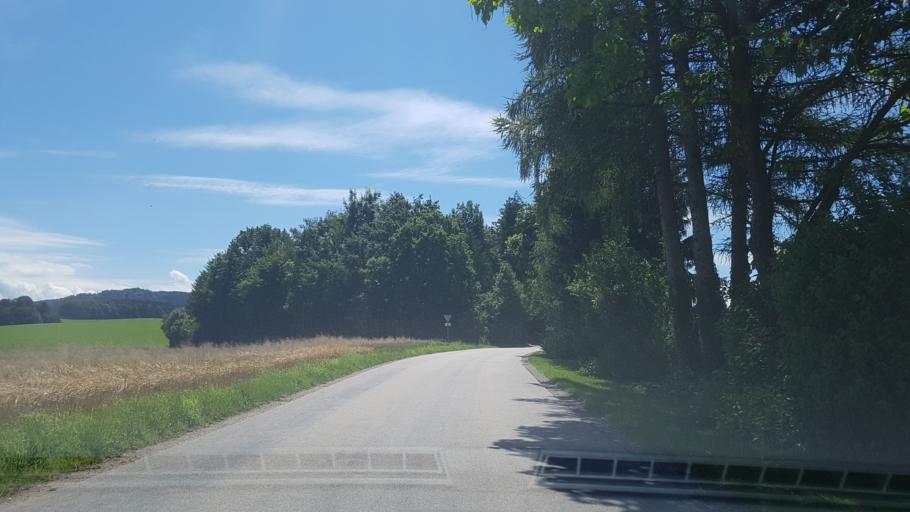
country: AT
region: Salzburg
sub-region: Politischer Bezirk Salzburg-Umgebung
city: Schleedorf
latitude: 48.0065
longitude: 13.1614
